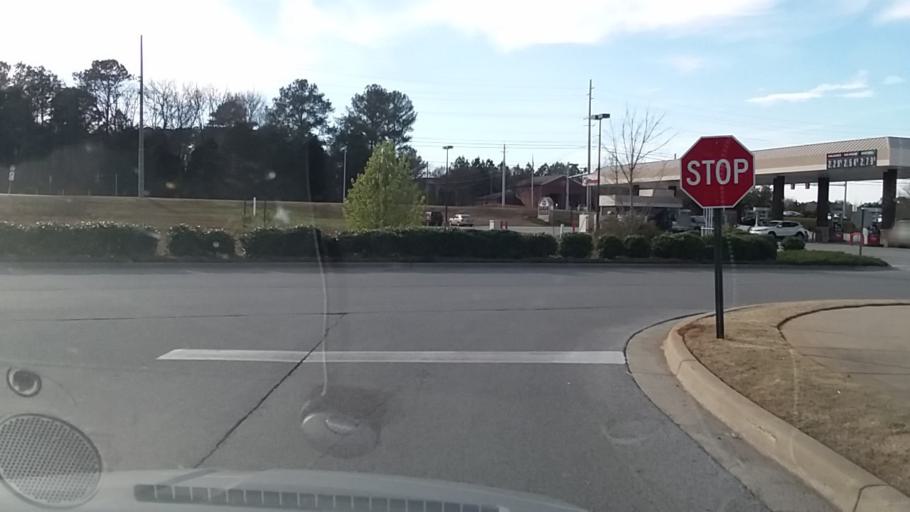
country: US
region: Alabama
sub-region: Madison County
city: Madison
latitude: 34.7569
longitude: -86.7131
